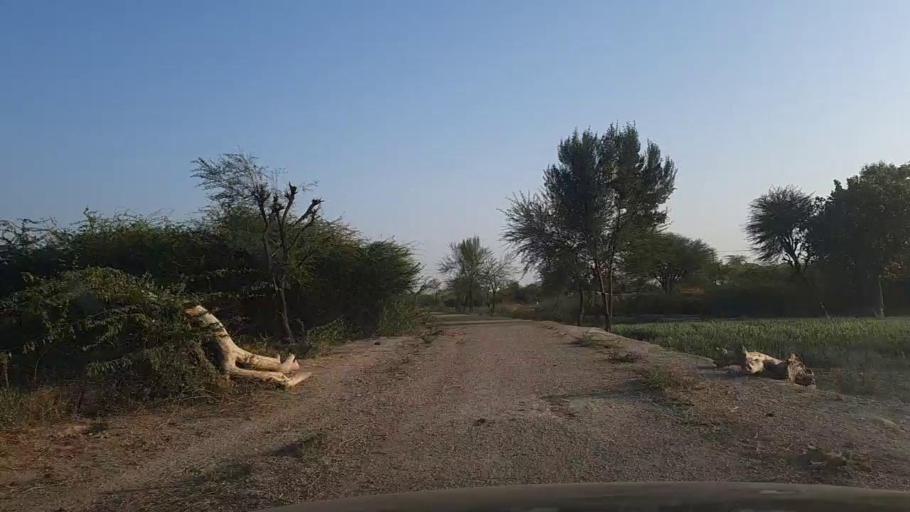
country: PK
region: Sindh
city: Naukot
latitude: 24.8921
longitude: 69.3457
